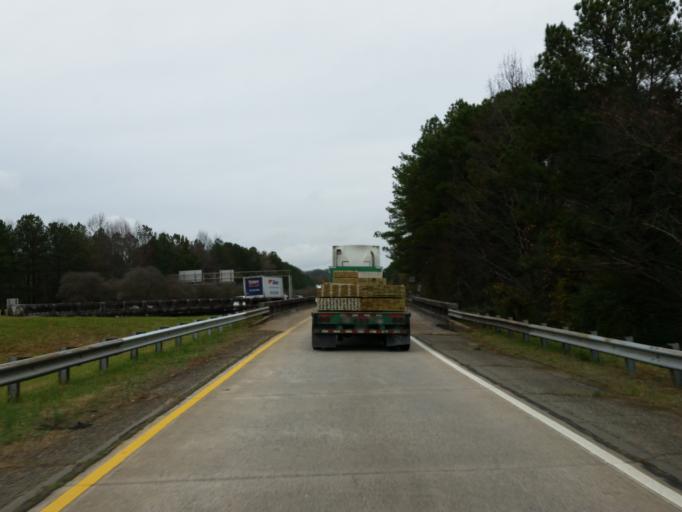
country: US
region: Georgia
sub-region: Cobb County
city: Marietta
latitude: 33.9871
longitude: -84.5385
